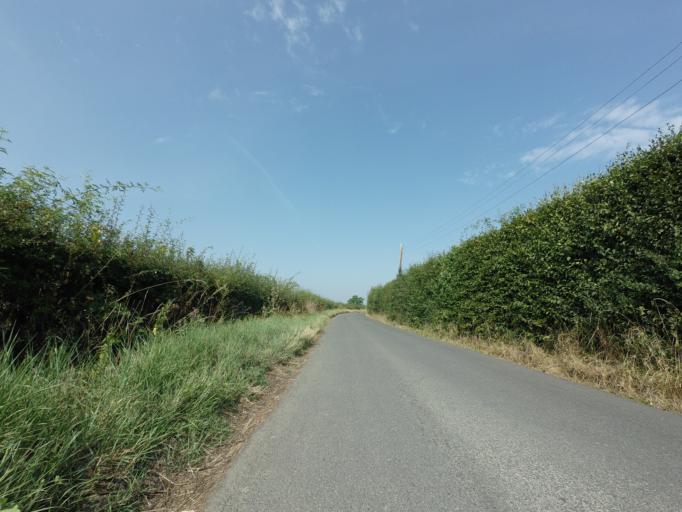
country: GB
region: England
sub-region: Kent
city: Staplehurst
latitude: 51.1269
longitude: 0.5824
